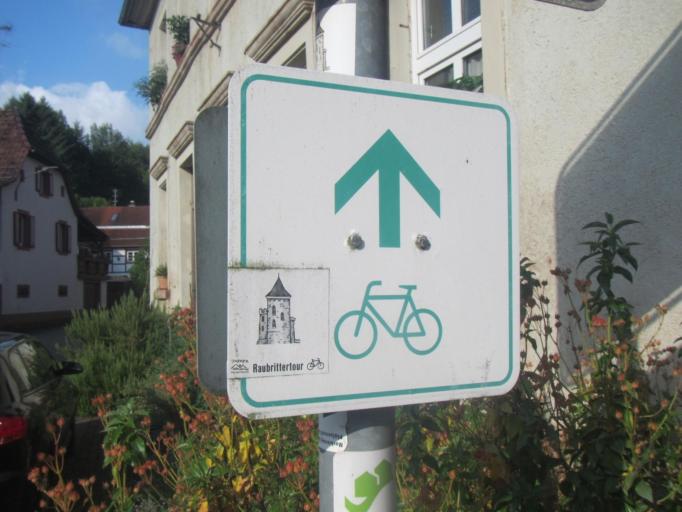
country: DE
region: Rheinland-Pfalz
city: Oberschlettenbach
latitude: 49.1455
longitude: 7.8711
